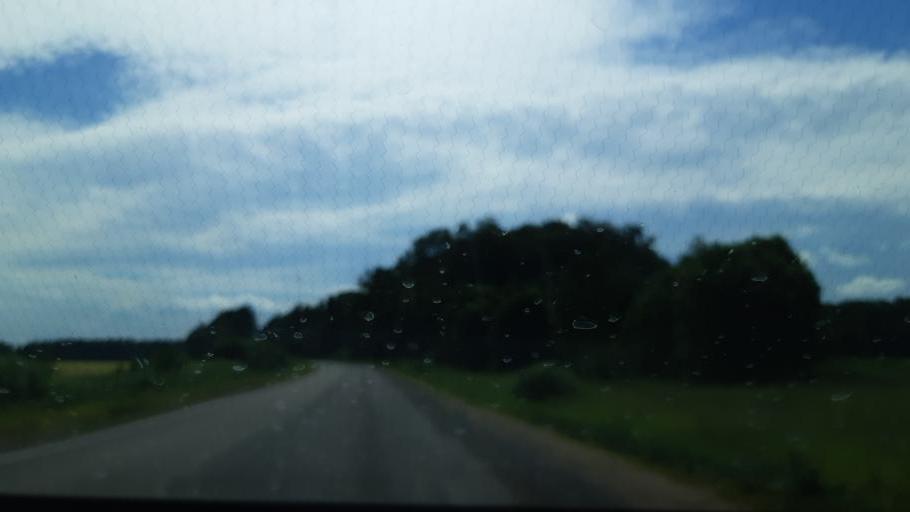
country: RU
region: Moskovskaya
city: Vereya
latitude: 55.2516
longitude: 36.0585
